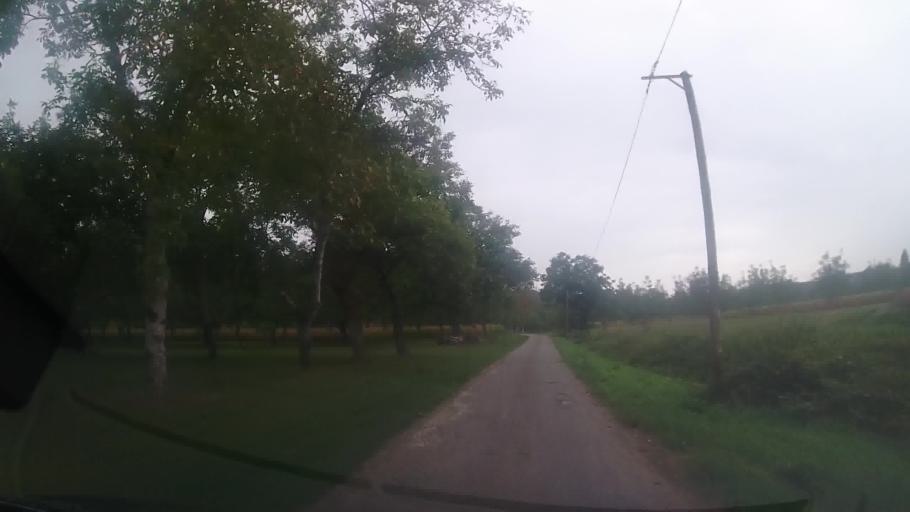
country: FR
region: Aquitaine
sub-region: Departement de la Dordogne
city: Cenac-et-Saint-Julien
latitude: 44.8040
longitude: 1.2008
